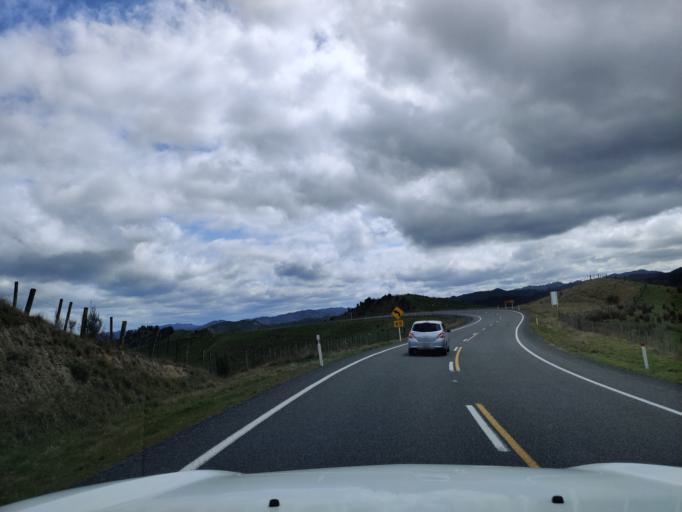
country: NZ
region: Manawatu-Wanganui
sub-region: Wanganui District
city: Wanganui
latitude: -39.7853
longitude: 175.2305
